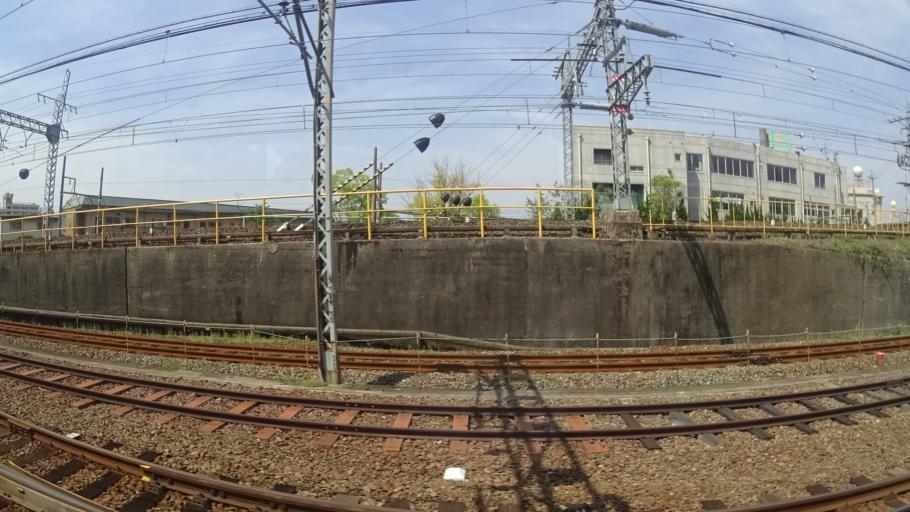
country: JP
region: Aichi
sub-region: Tsushima-shi
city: Tsushima
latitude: 35.0703
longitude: 136.6839
